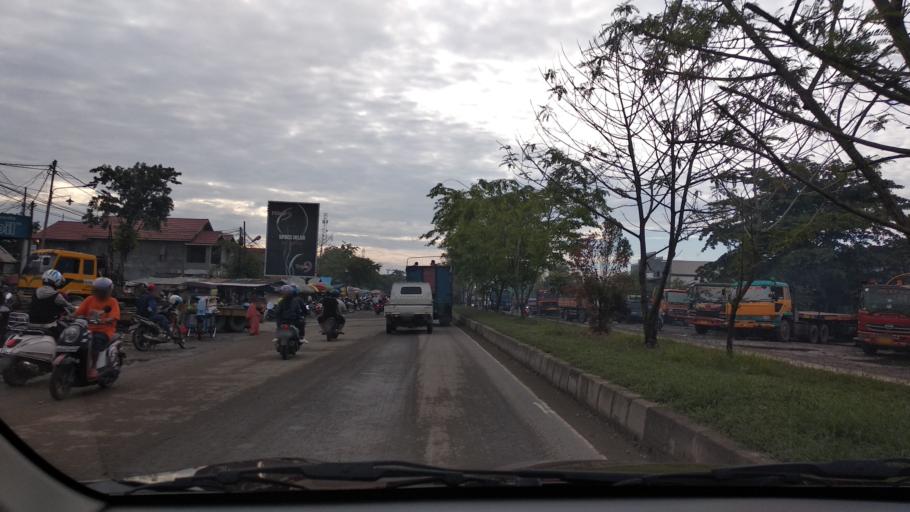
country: ID
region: South Kalimantan
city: Banjarmasin
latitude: -3.3312
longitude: 114.5613
